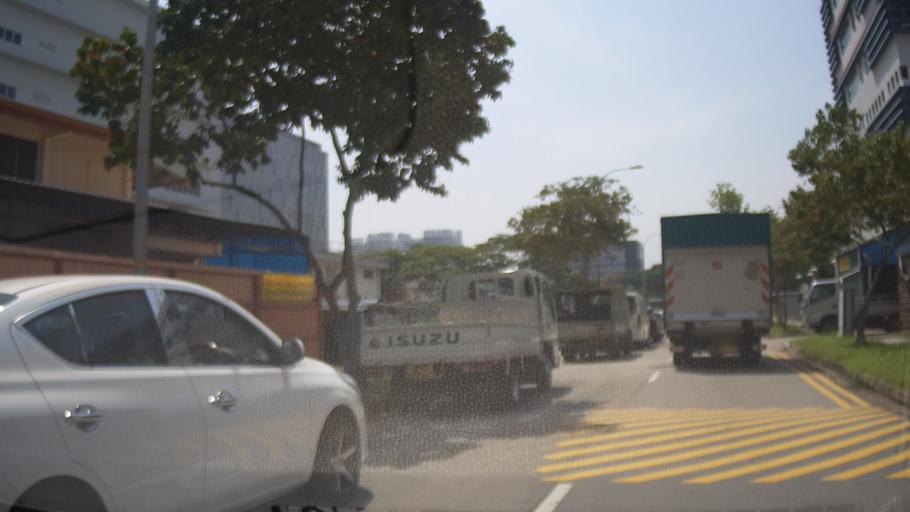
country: SG
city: Singapore
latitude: 1.3150
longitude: 103.8629
